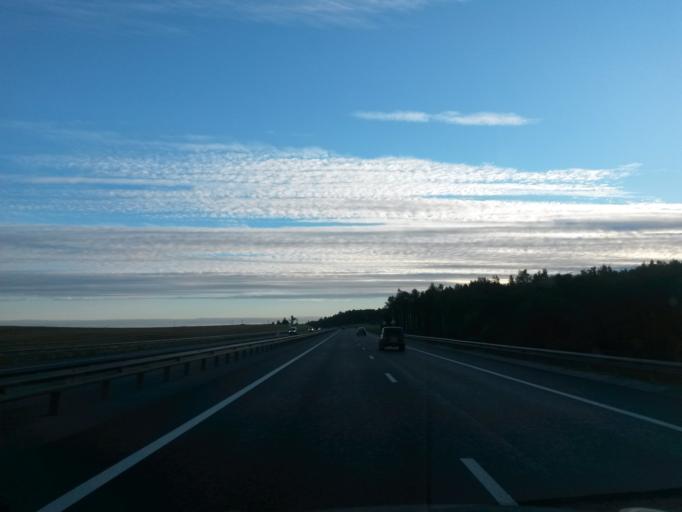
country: RU
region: Moskovskaya
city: Krasnozavodsk
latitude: 56.4247
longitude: 38.3370
